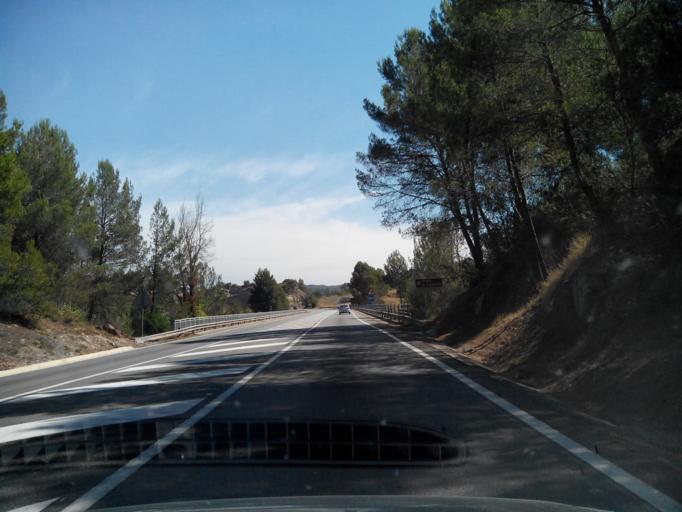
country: ES
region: Catalonia
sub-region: Provincia de Barcelona
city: Monistrol de Montserrat
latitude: 41.6413
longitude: 1.8548
